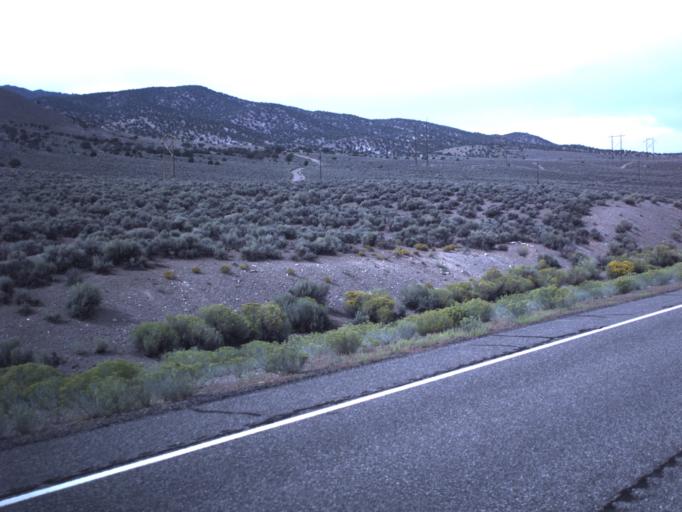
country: US
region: Utah
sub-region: Piute County
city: Junction
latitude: 38.3035
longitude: -112.2238
